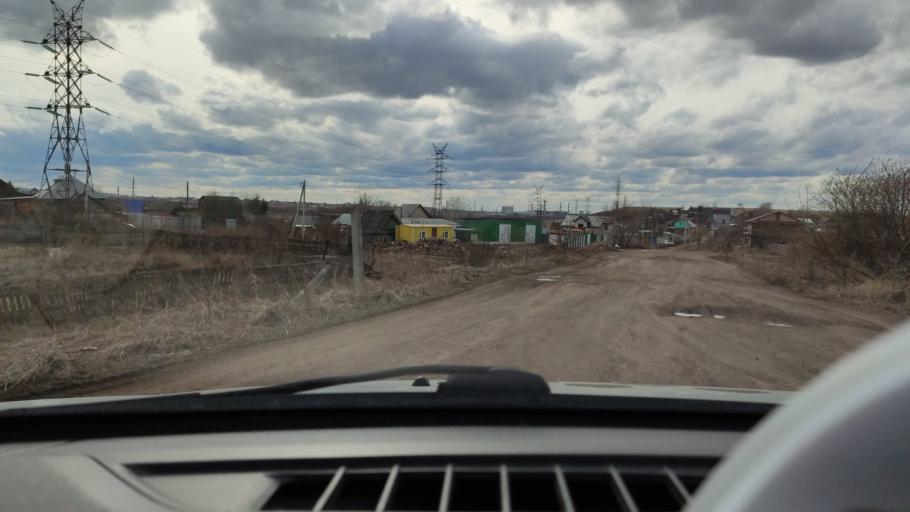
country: RU
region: Perm
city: Froly
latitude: 57.9300
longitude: 56.2398
